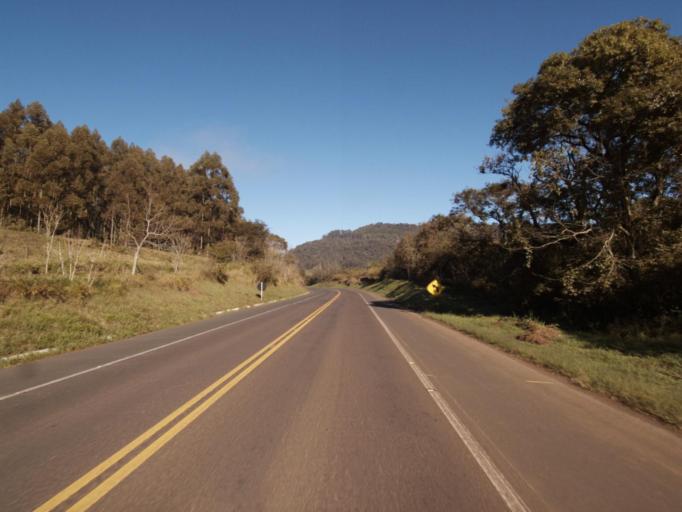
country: BR
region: Rio Grande do Sul
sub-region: Frederico Westphalen
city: Frederico Westphalen
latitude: -26.9852
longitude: -53.2246
